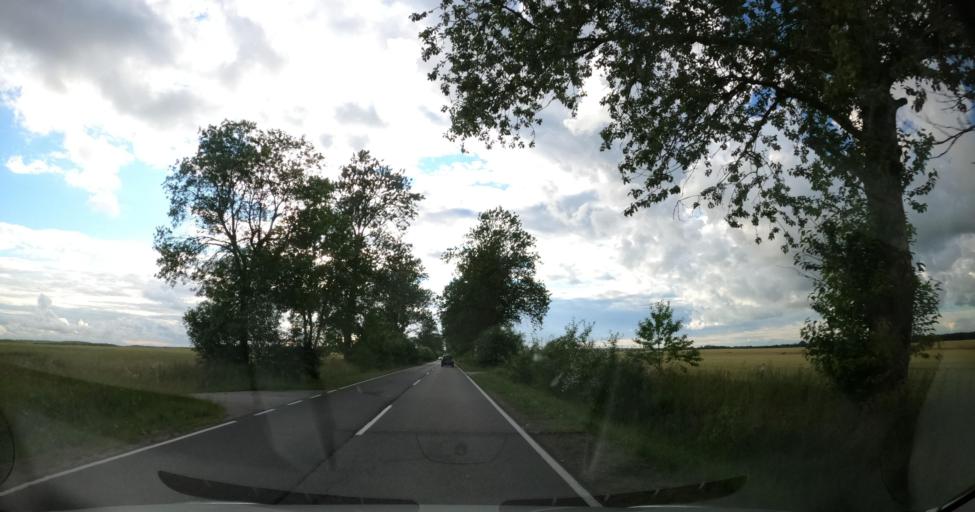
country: PL
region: Pomeranian Voivodeship
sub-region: Powiat slupski
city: Potegowo
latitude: 54.4249
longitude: 17.3737
